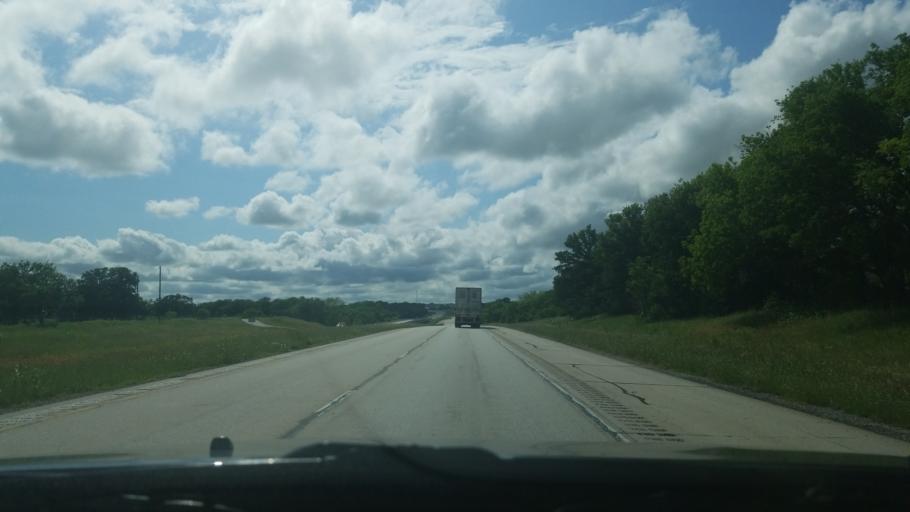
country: US
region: Texas
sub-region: Denton County
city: Ponder
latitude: 33.2482
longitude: -97.3990
